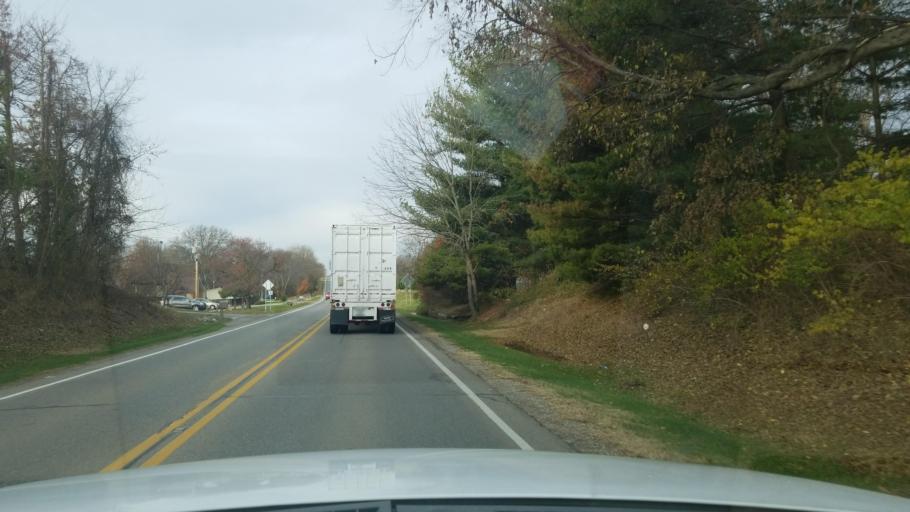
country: US
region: Indiana
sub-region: Posey County
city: Mount Vernon
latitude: 37.9290
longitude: -87.9261
